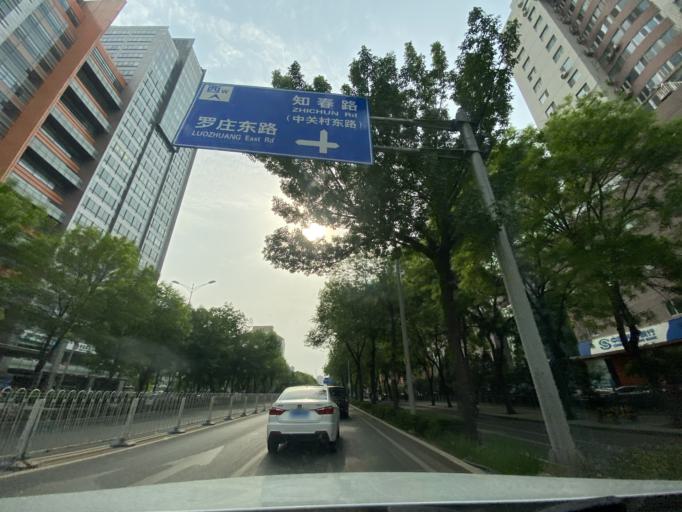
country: CN
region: Beijing
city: Qinghe
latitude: 39.9752
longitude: 116.3432
